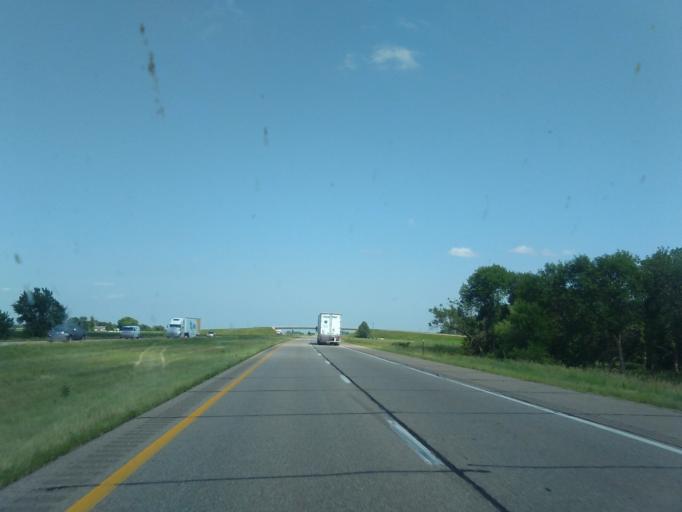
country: US
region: Nebraska
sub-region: Phelps County
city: Holdrege
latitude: 40.6908
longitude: -99.3478
